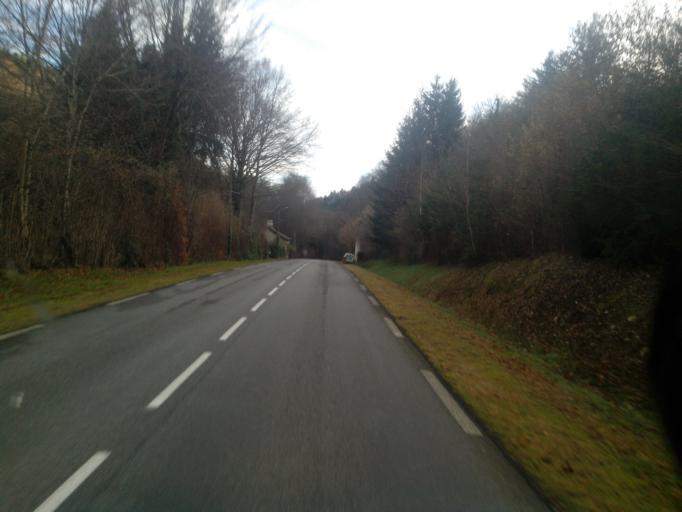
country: FR
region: Limousin
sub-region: Departement de la Haute-Vienne
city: Eymoutiers
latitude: 45.6804
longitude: 1.7957
